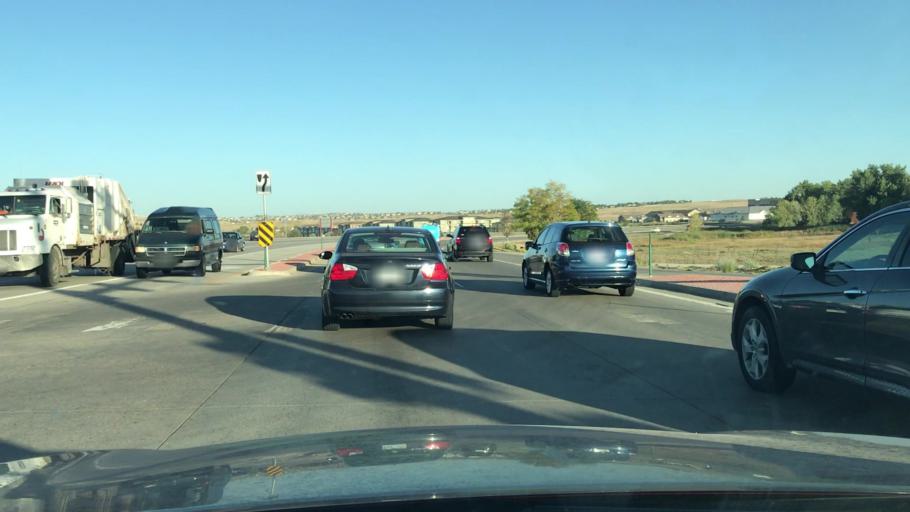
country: US
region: Colorado
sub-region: Boulder County
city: Lafayette
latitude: 39.9779
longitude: -105.0938
